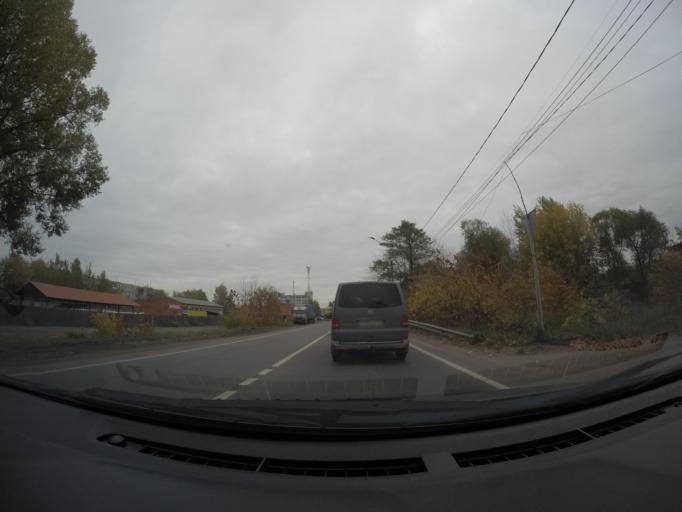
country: RU
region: Moskovskaya
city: Imeni Vorovskogo
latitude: 55.7222
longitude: 38.3363
